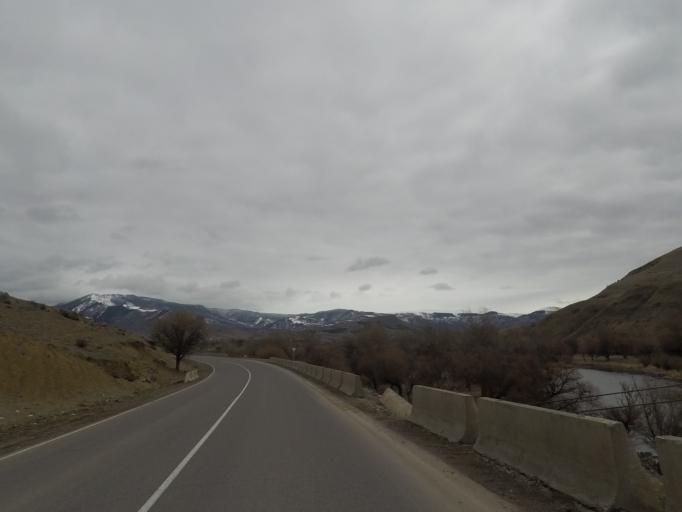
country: GE
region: Samtskhe-Javakheti
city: Aspindza
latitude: 41.5949
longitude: 43.2121
